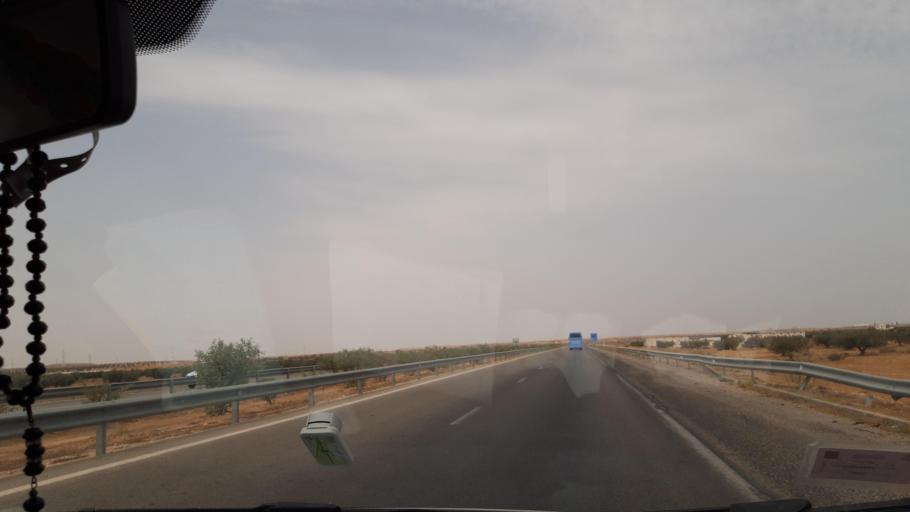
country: TN
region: Safaqis
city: Sfax
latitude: 34.7325
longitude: 10.5926
